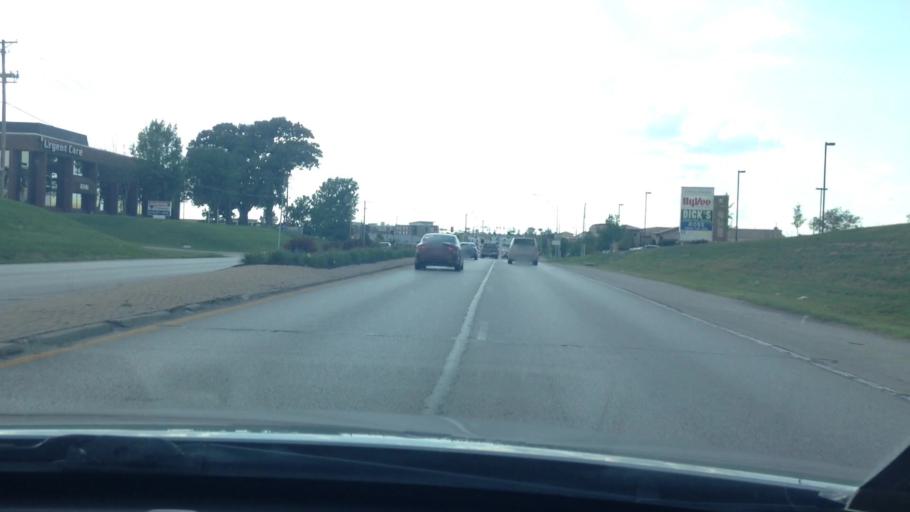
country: US
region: Missouri
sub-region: Clay County
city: Liberty
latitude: 39.2446
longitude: -94.4463
